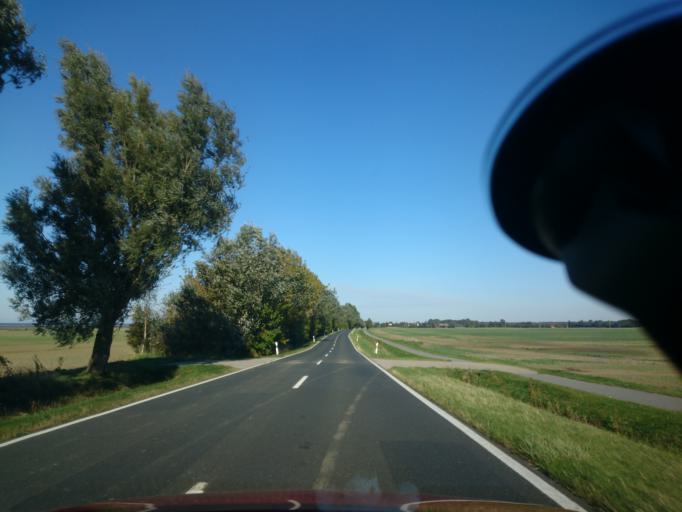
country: DE
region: Mecklenburg-Vorpommern
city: Saal
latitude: 54.3233
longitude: 12.5085
